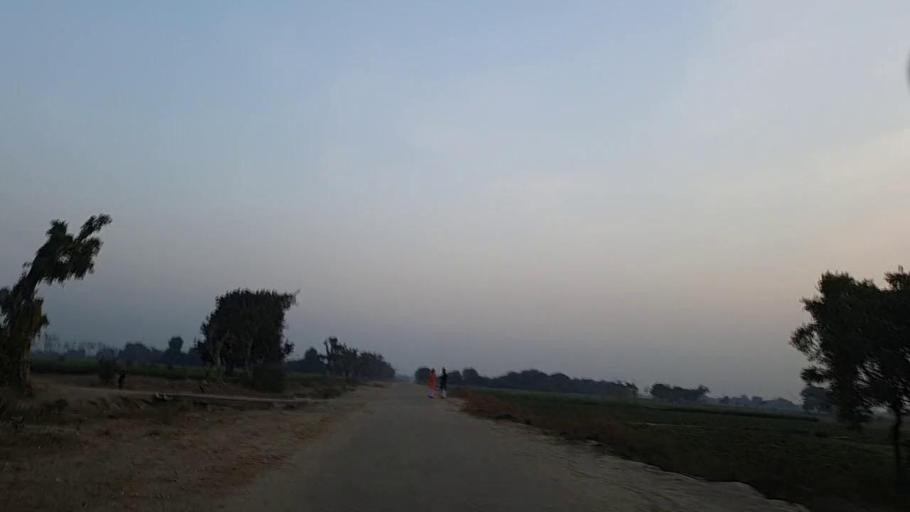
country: PK
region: Sindh
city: Tando Ghulam Ali
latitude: 25.1214
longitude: 68.8984
